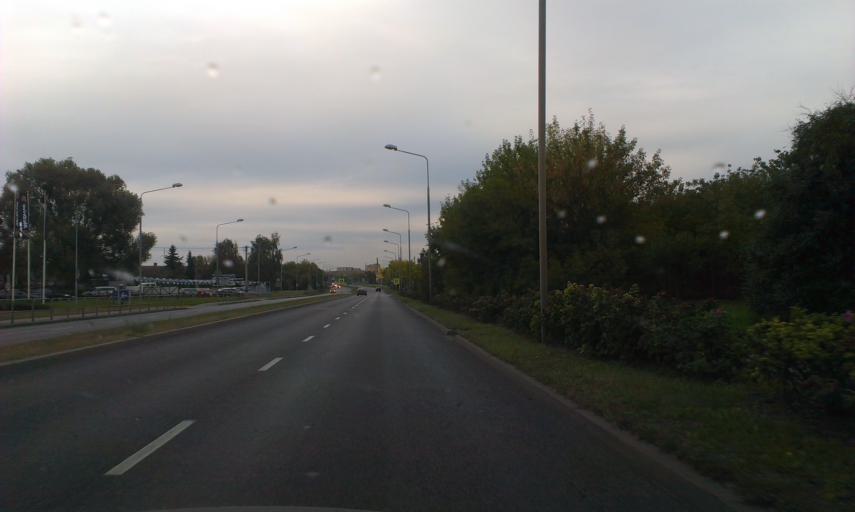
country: PL
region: Masovian Voivodeship
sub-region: Radom
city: Radom
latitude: 51.4171
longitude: 21.1363
